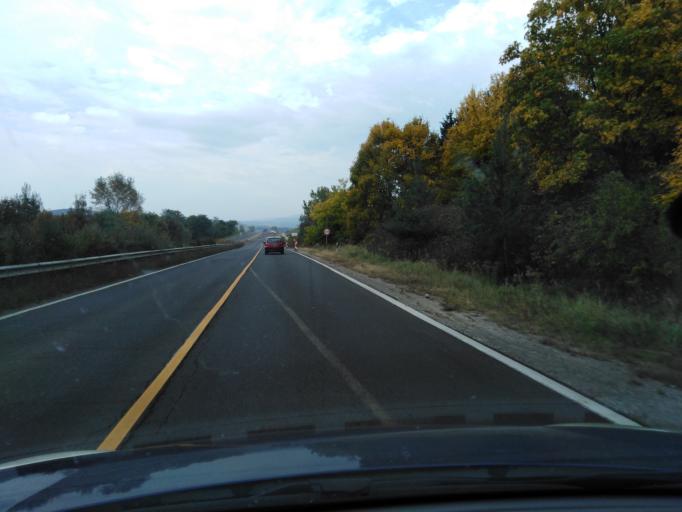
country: HU
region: Nograd
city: Kazar
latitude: 48.0311
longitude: 19.8087
